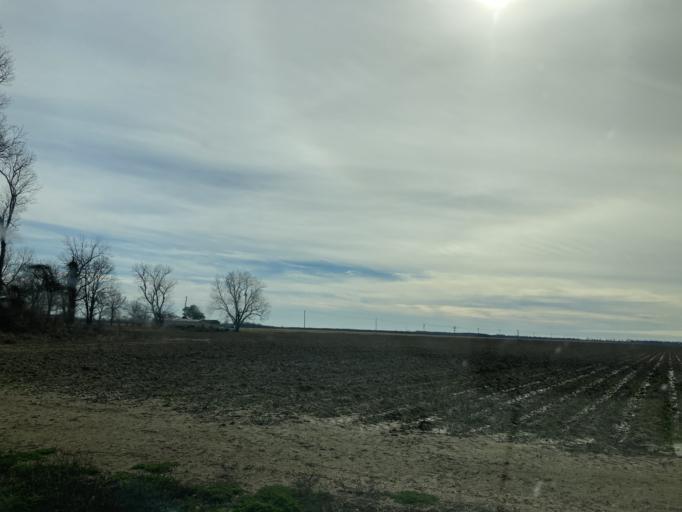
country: US
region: Mississippi
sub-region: Humphreys County
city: Belzoni
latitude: 33.1164
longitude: -90.6149
